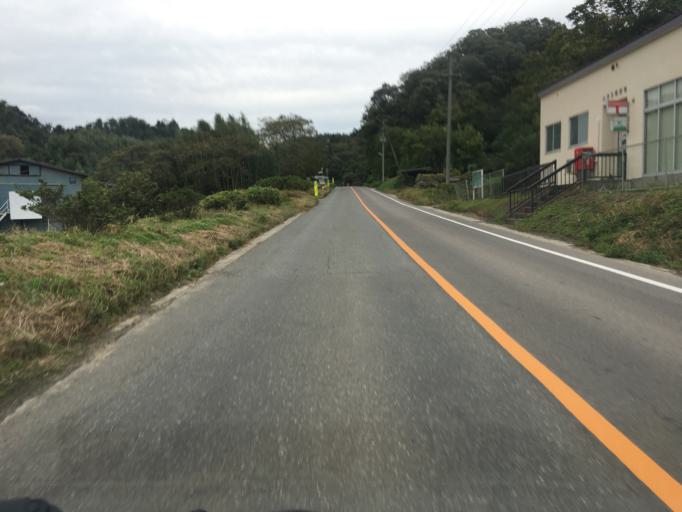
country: JP
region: Fukushima
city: Yanagawamachi-saiwaicho
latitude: 37.8771
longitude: 140.6633
